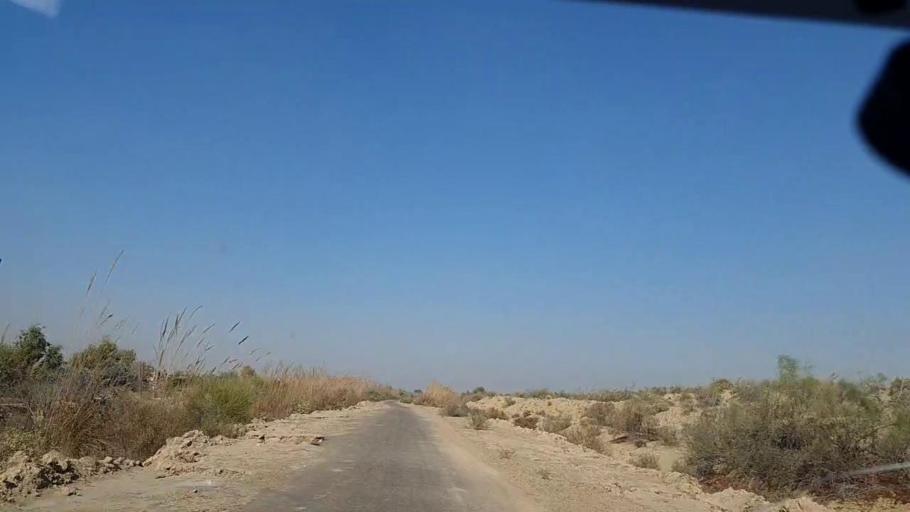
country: PK
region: Sindh
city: Khanpur
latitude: 27.5860
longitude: 69.3761
